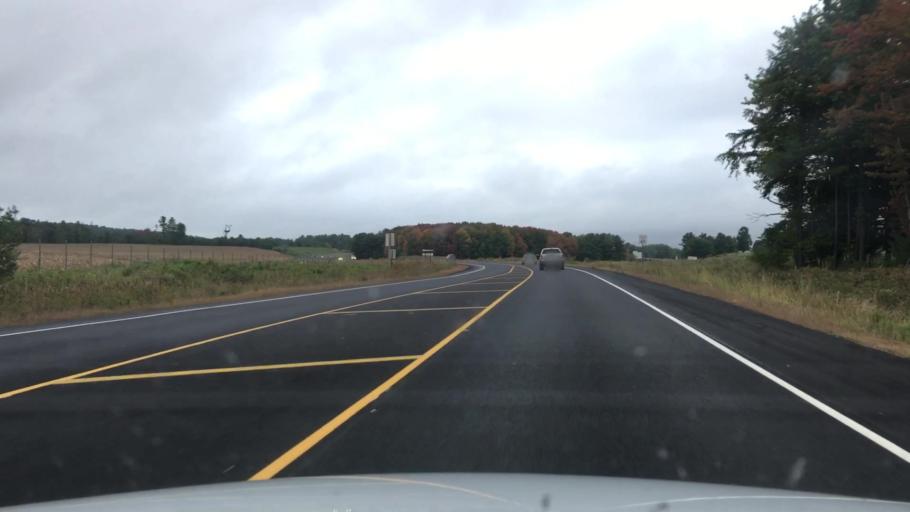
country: US
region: Maine
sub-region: Cumberland County
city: New Gloucester
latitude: 43.8873
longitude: -70.3410
